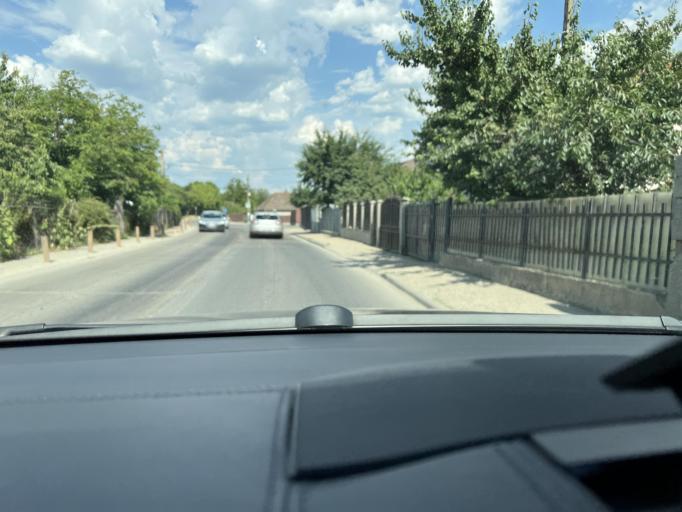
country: RO
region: Cluj
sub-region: Comuna Apahida
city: Dezmir
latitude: 46.7783
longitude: 23.6652
